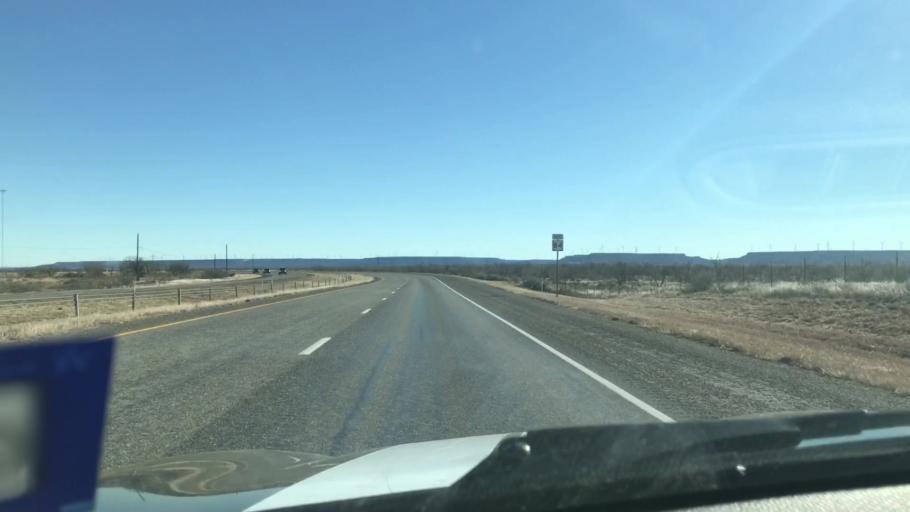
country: US
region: Texas
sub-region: Garza County
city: Post
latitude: 33.0765
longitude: -101.2381
